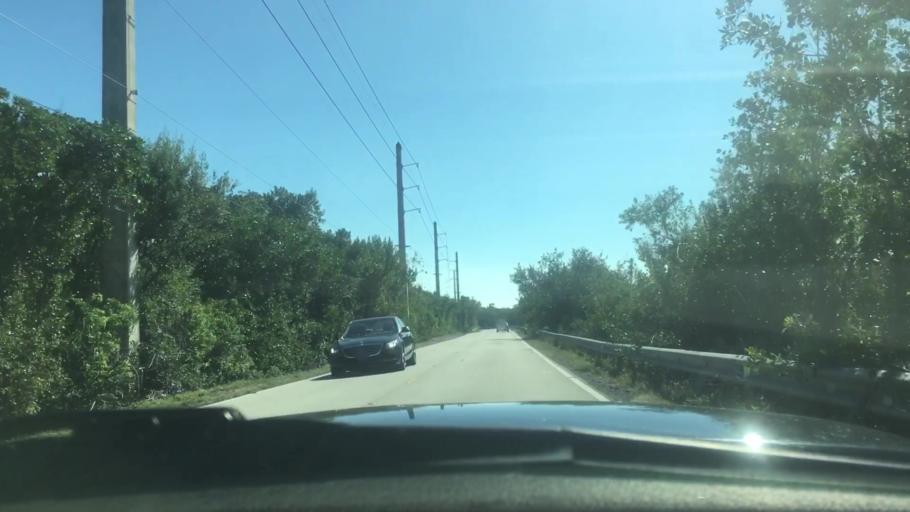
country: US
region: Florida
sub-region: Monroe County
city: North Key Largo
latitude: 25.2943
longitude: -80.3830
